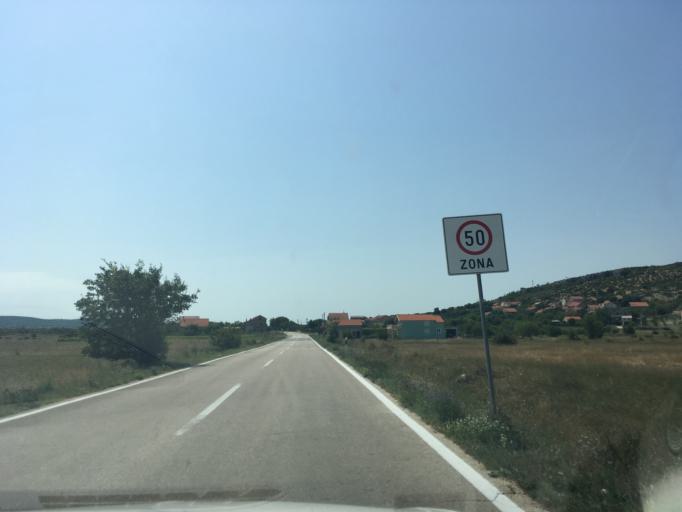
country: HR
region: Zadarska
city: Benkovac
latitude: 43.9635
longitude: 15.7560
